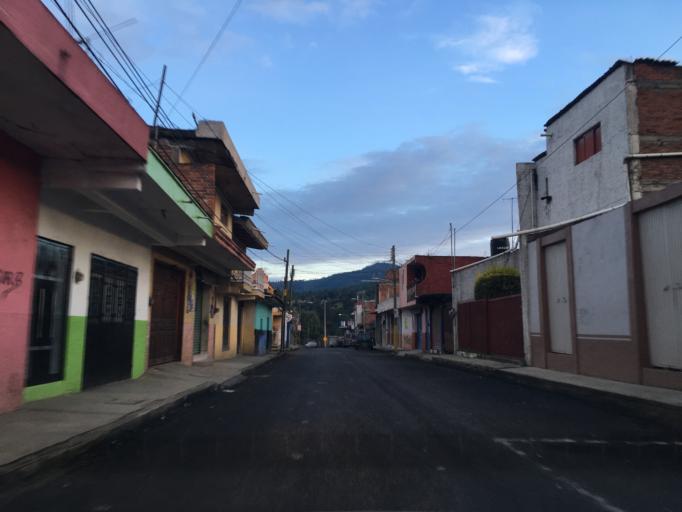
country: MX
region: Michoacan
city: Cheran
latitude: 19.6888
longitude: -101.9549
